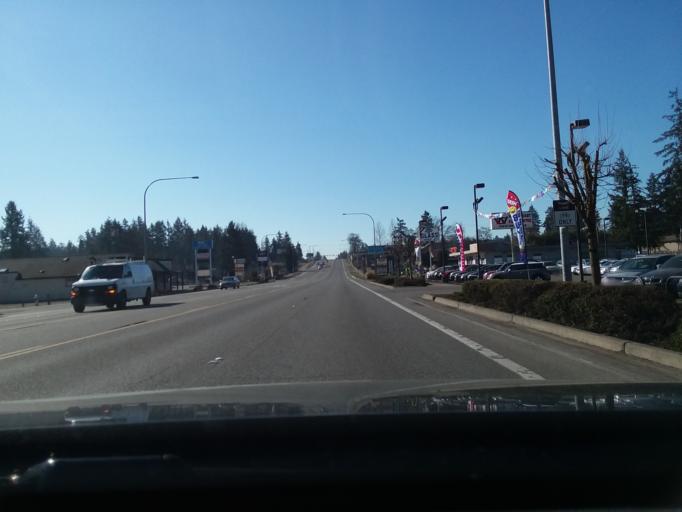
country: US
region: Washington
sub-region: Pierce County
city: Parkland
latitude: 47.1301
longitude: -122.4348
